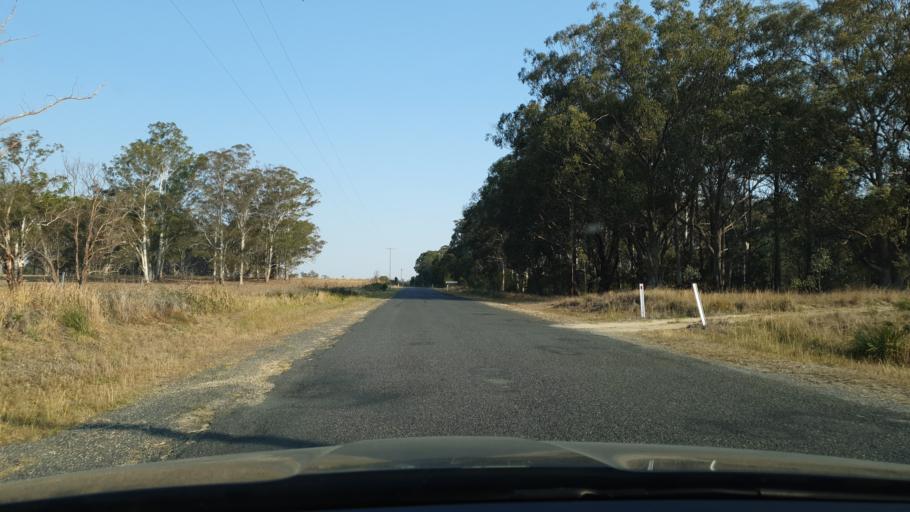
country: AU
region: New South Wales
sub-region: Tenterfield Municipality
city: Carrolls Creek
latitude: -28.6903
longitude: 152.0874
